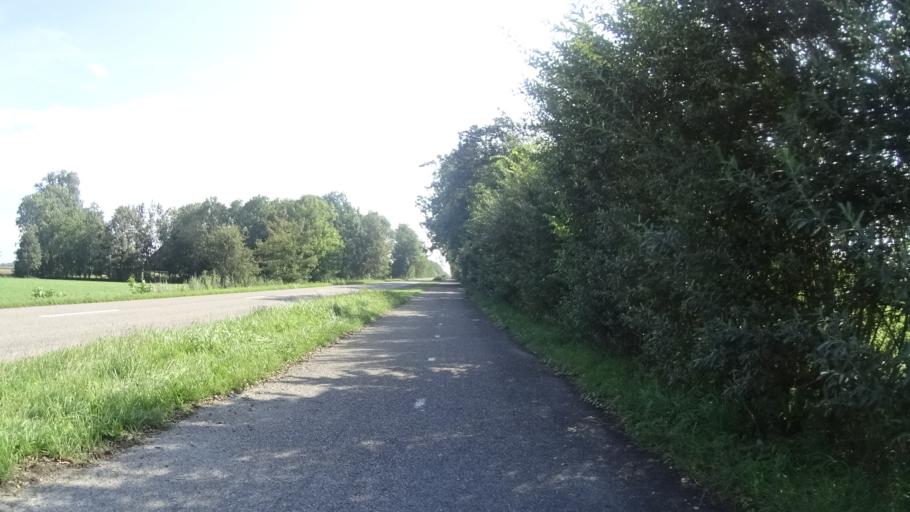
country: NL
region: Friesland
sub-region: Gemeente Franekeradeel
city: Tzum
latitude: 53.1909
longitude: 5.5810
